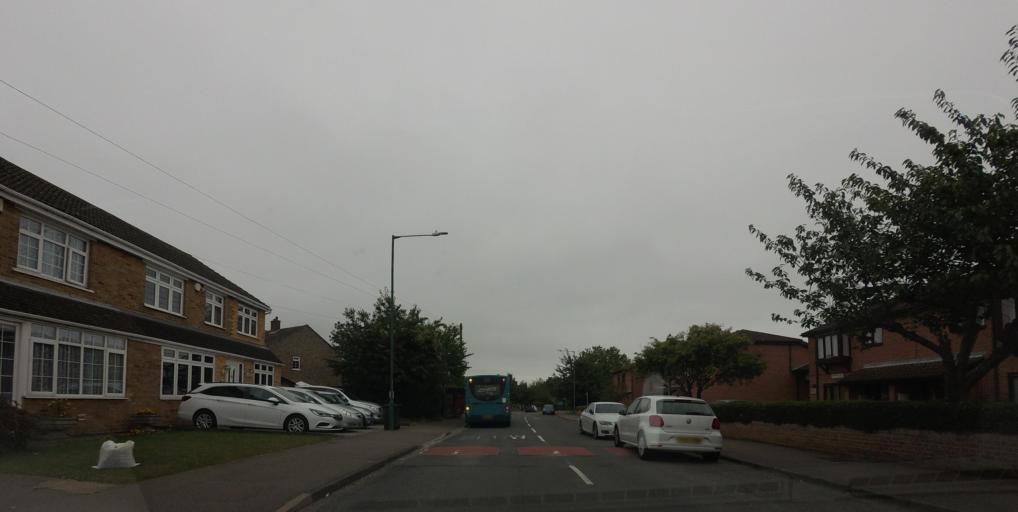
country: GB
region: England
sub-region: Kent
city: Stone
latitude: 51.4352
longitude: 0.2474
